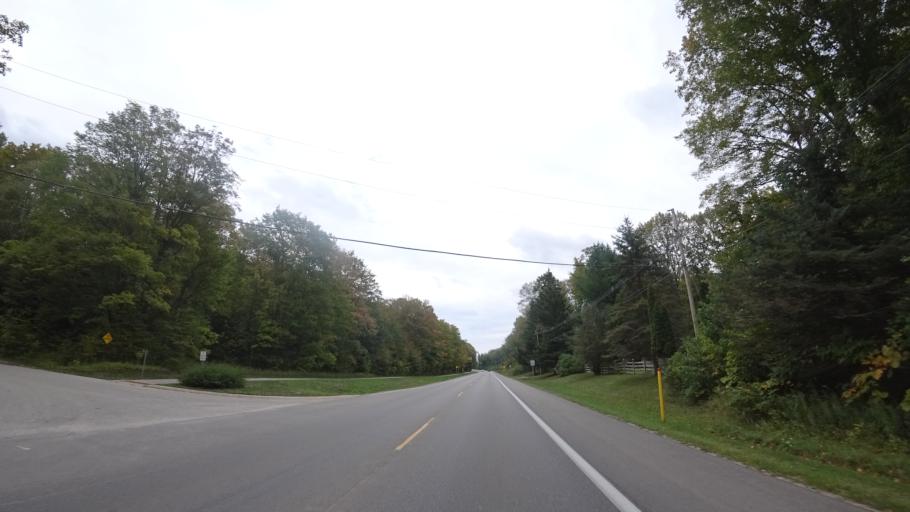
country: US
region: Michigan
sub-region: Emmet County
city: Petoskey
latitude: 45.4290
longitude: -84.9226
